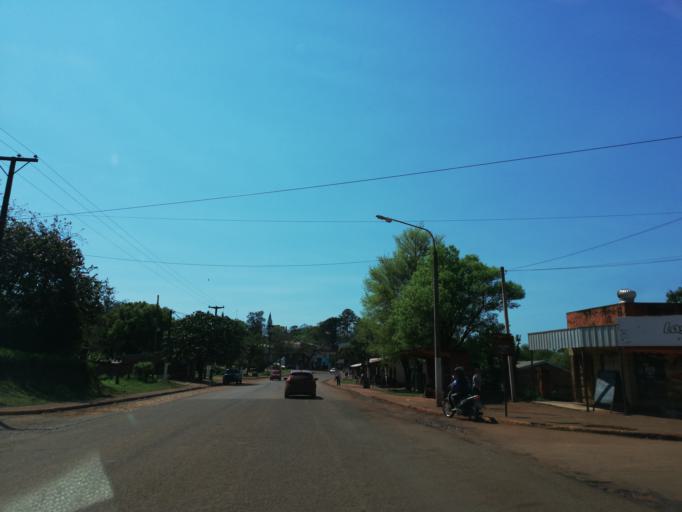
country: AR
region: Misiones
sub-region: Departamento de Eldorado
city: Eldorado
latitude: -26.4066
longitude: -54.6557
